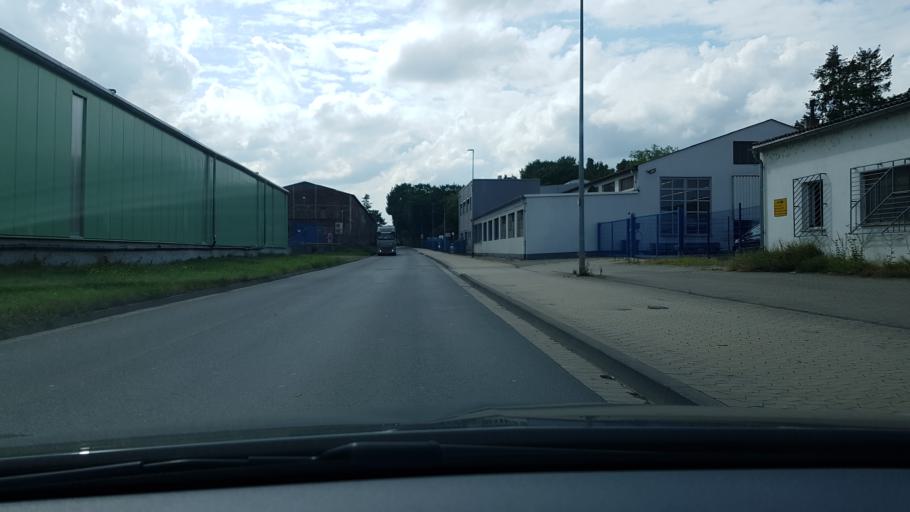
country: DE
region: Rheinland-Pfalz
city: Andernach
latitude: 50.4388
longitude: 7.4254
